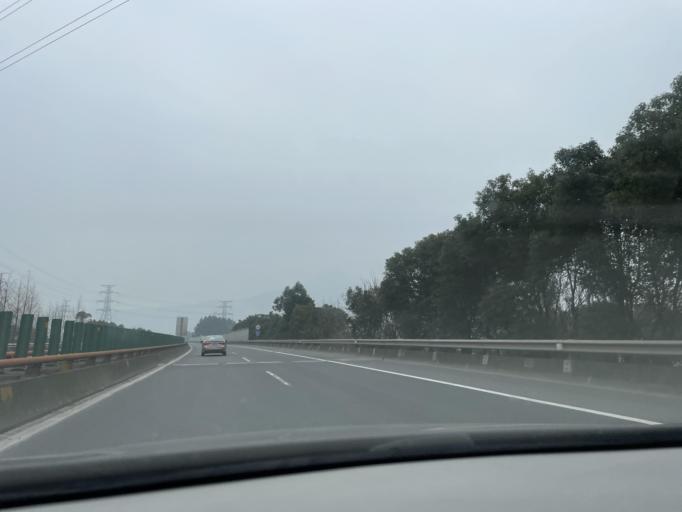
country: CN
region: Zhejiang Sheng
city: Shiqiao
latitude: 27.9653
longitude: 120.5934
